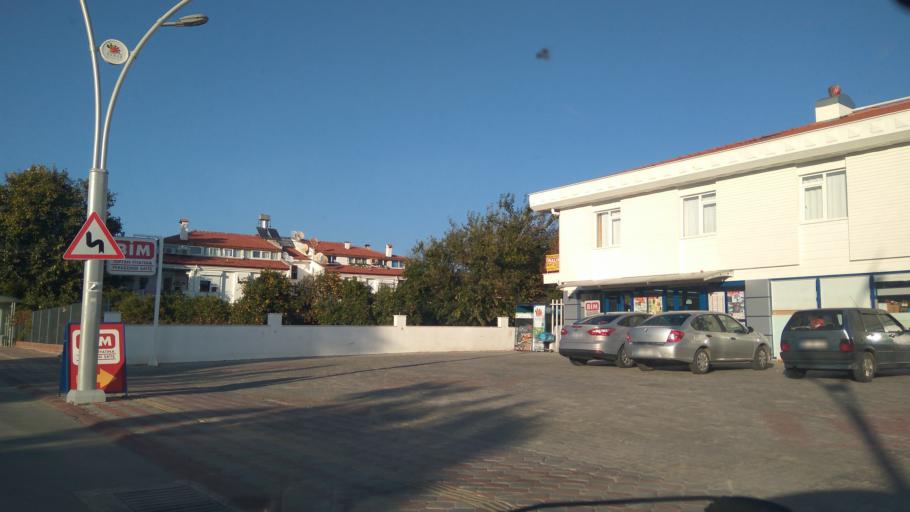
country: TR
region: Antalya
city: Kemer
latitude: 36.5657
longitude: 30.5585
